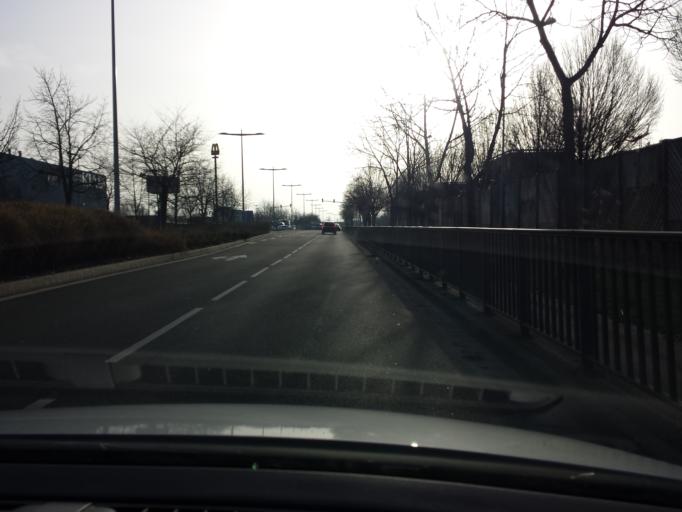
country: FR
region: Haute-Normandie
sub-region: Departement de l'Eure
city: Evreux
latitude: 49.0132
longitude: 1.1689
